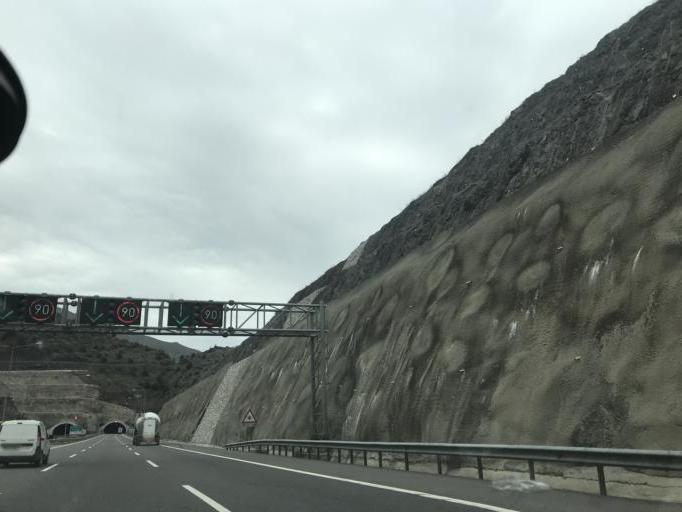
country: TR
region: Nigde
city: Ciftehan
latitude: 37.5557
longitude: 34.7690
